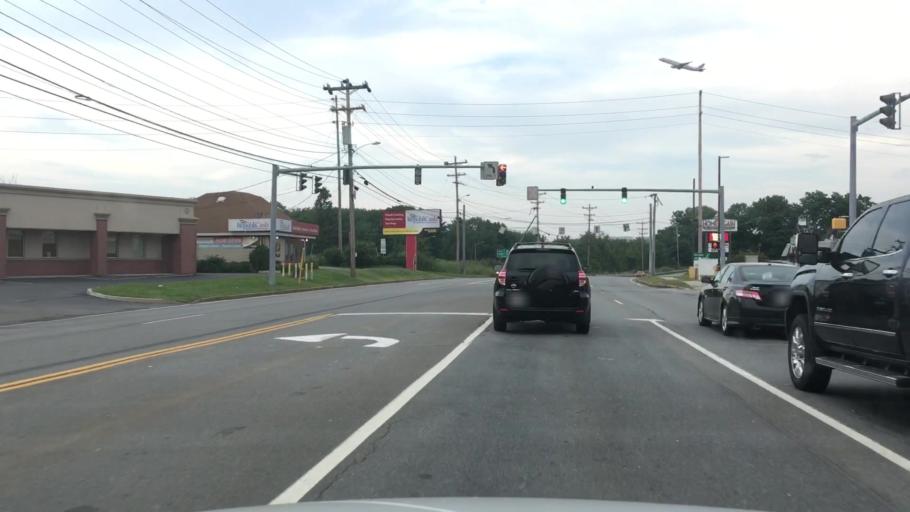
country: US
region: Maine
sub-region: Cumberland County
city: South Portland Gardens
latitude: 43.6401
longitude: -70.3343
